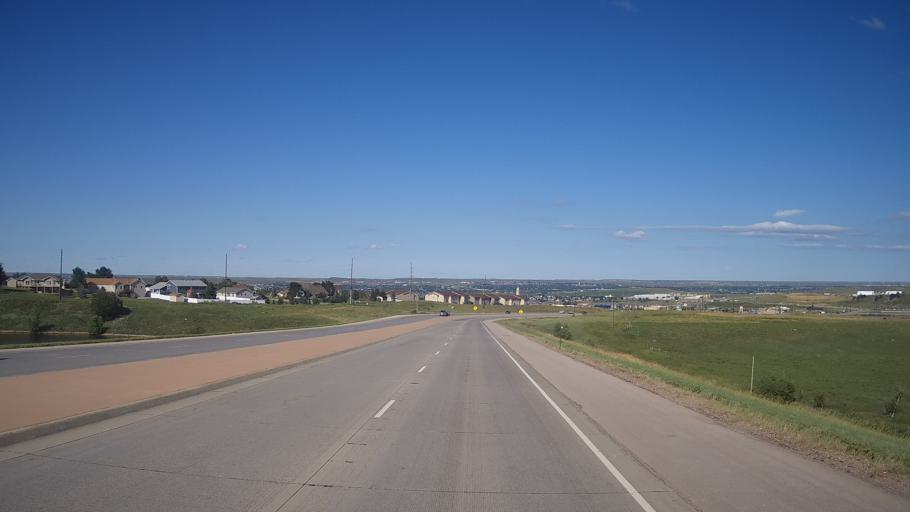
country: US
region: South Dakota
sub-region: Pennington County
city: Rapid City
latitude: 44.0293
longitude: -103.2293
